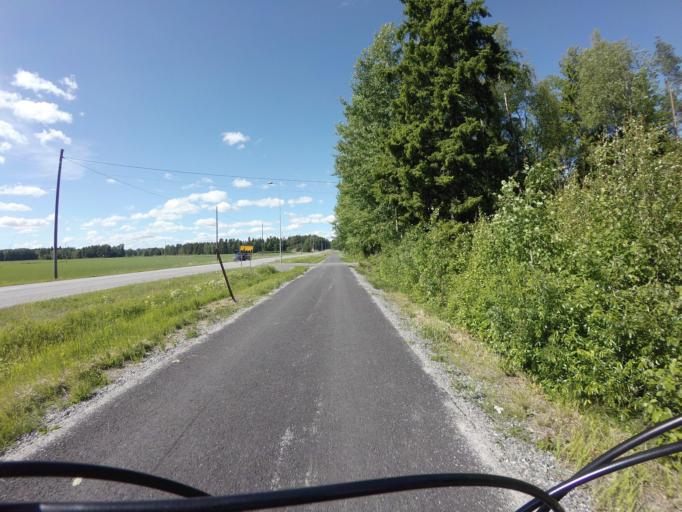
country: FI
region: Varsinais-Suomi
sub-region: Turku
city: Vahto
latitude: 60.5265
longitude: 22.2926
